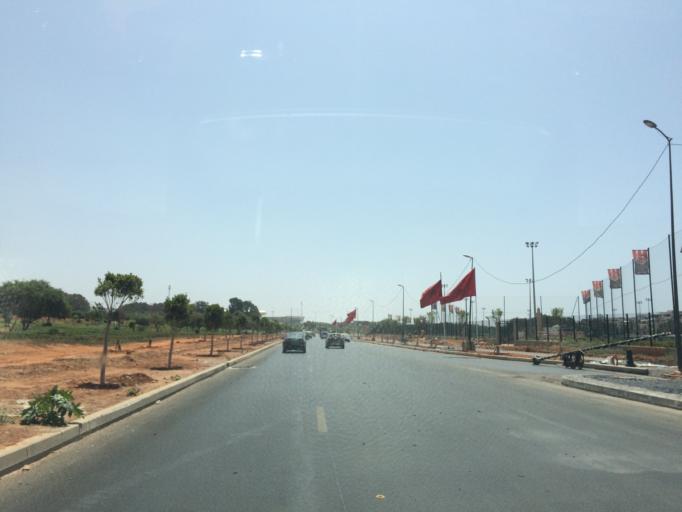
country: MA
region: Rabat-Sale-Zemmour-Zaer
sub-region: Skhirate-Temara
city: Temara
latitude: 33.9716
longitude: -6.8812
